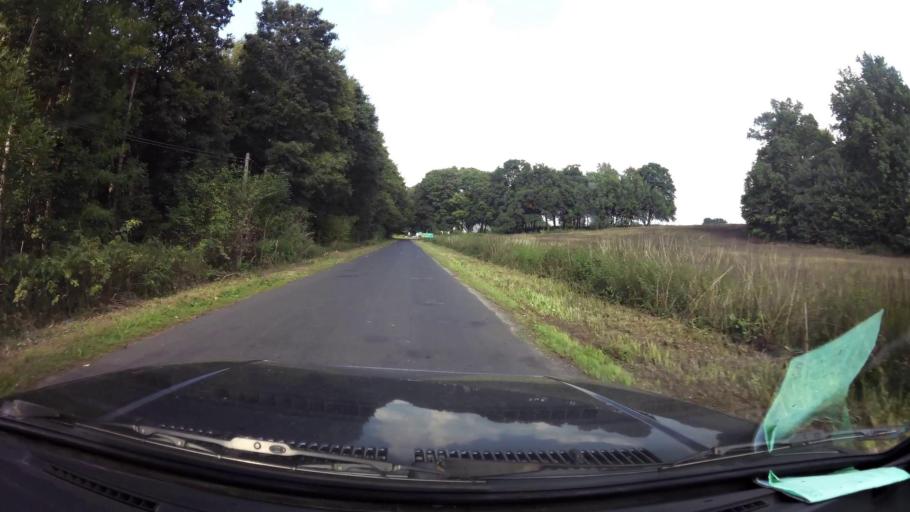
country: PL
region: West Pomeranian Voivodeship
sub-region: Powiat koszalinski
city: Polanow
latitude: 54.1367
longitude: 16.5230
